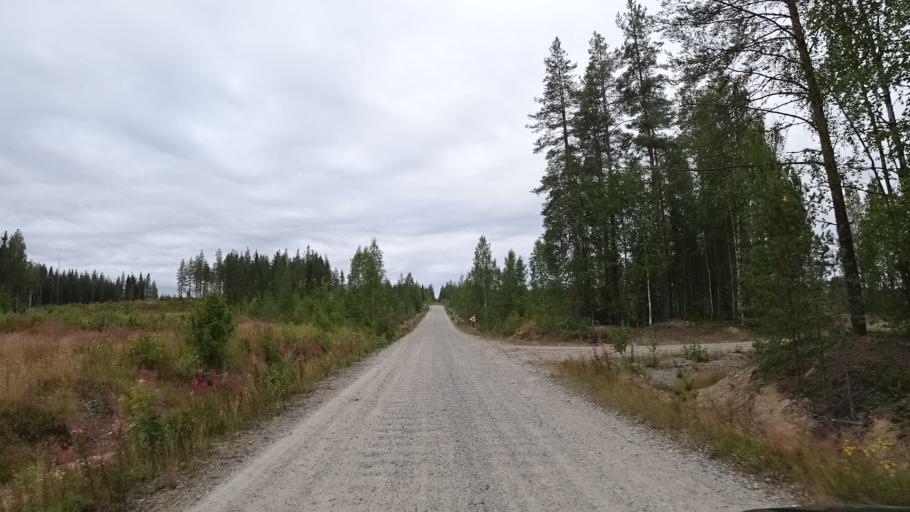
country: FI
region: North Karelia
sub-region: Joensuu
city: Ilomantsi
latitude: 63.1554
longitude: 30.6311
